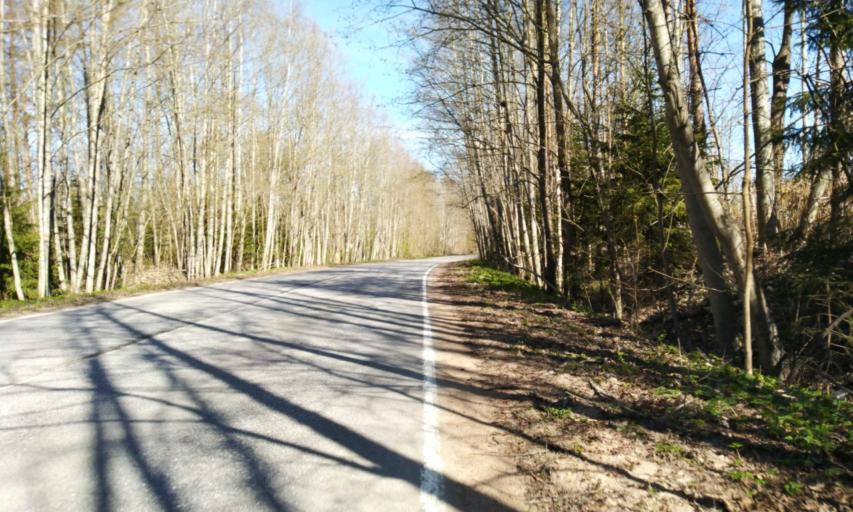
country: RU
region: Leningrad
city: Garbolovo
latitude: 60.4113
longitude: 30.4583
